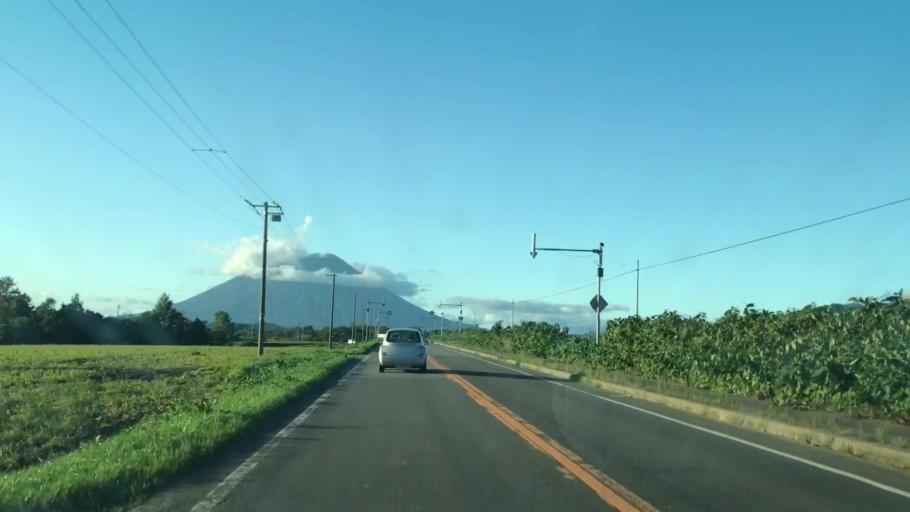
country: JP
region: Hokkaido
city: Niseko Town
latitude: 42.6755
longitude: 140.8419
